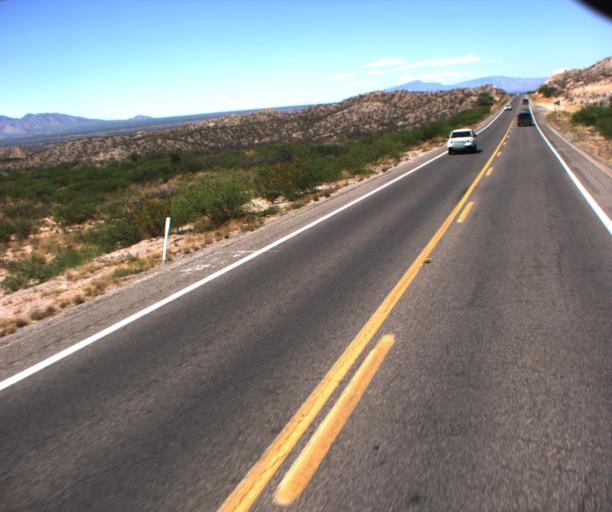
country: US
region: Arizona
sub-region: Cochise County
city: Saint David
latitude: 31.8232
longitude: -110.1747
